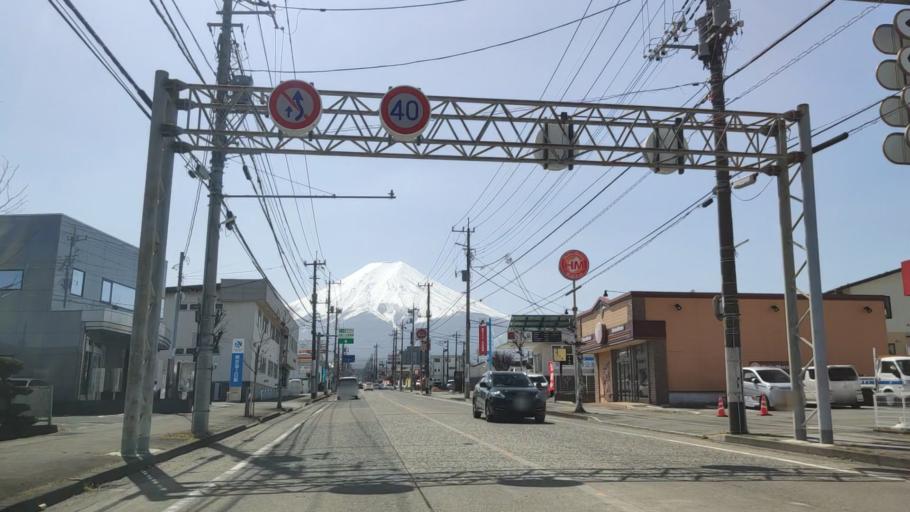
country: JP
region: Yamanashi
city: Fujikawaguchiko
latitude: 35.4823
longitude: 138.8040
